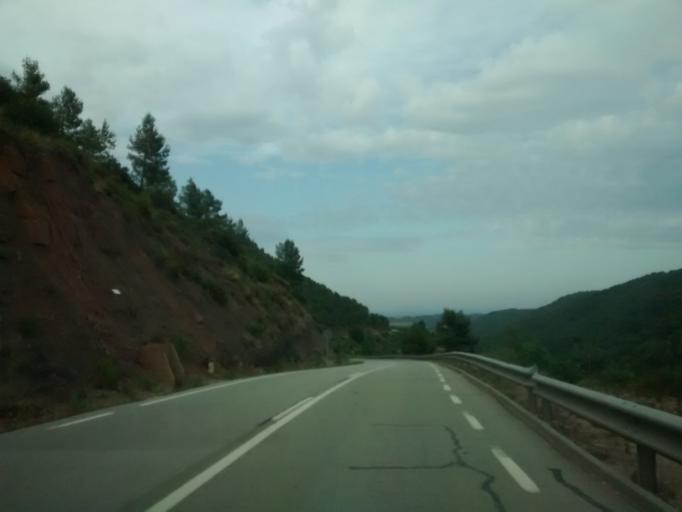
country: ES
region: Catalonia
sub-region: Provincia de Barcelona
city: Fonollosa
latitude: 41.7605
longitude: 1.6886
